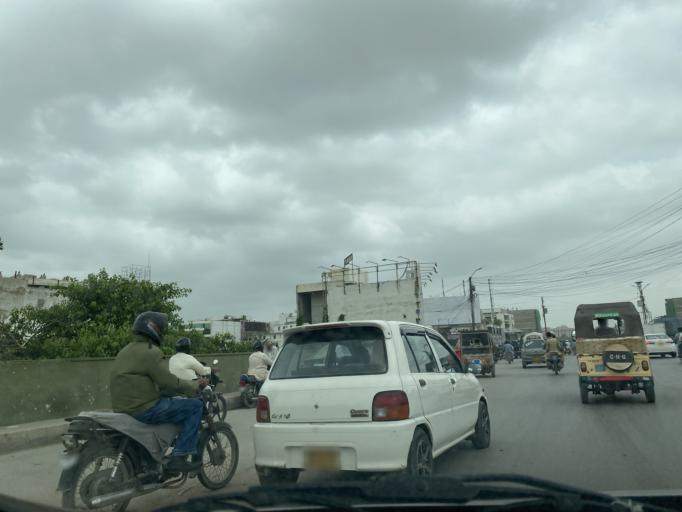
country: PK
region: Sindh
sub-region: Karachi District
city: Karachi
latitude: 24.8664
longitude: 67.0836
